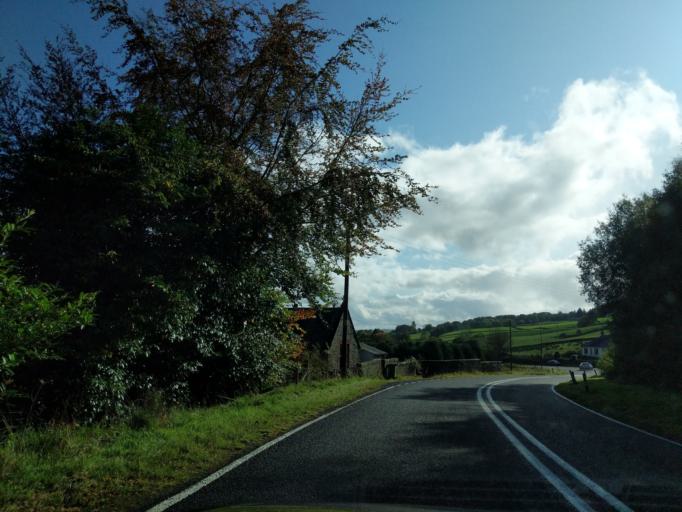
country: GB
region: Scotland
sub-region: Dumfries and Galloway
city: Moffat
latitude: 55.3402
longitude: -3.4572
